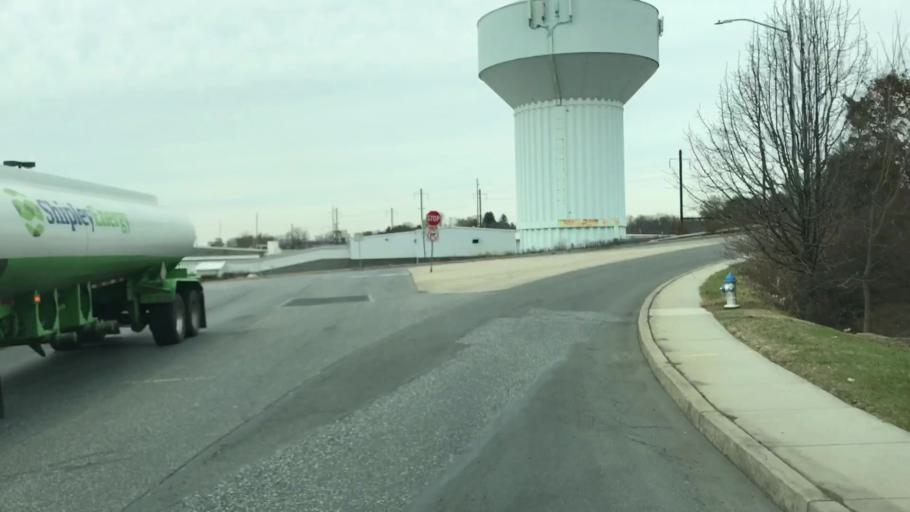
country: US
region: Pennsylvania
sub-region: Dauphin County
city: Middletown
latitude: 40.1949
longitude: -76.7390
